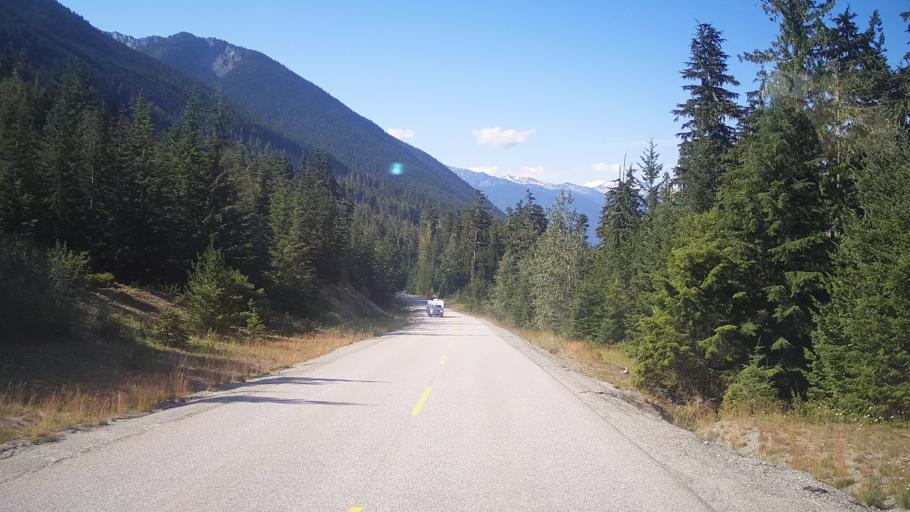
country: CA
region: British Columbia
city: Pemberton
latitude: 50.3496
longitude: -122.5330
